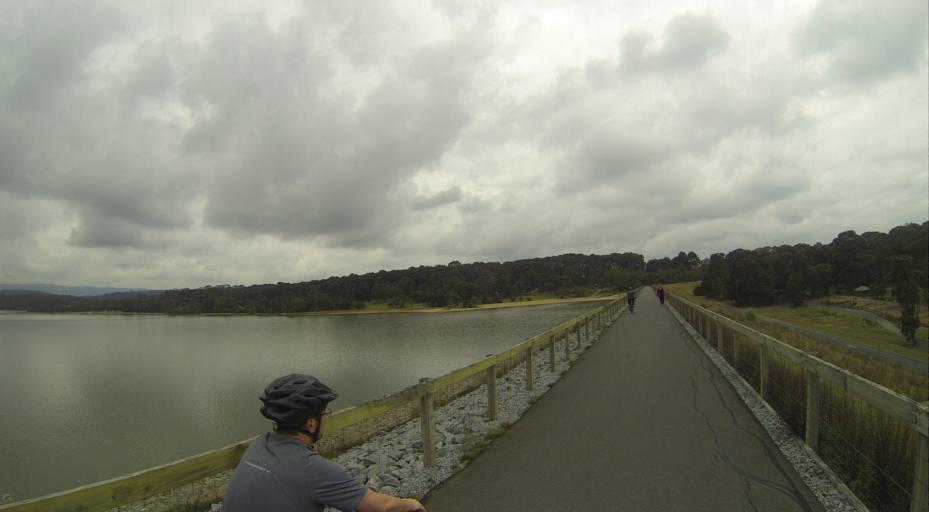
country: AU
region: Victoria
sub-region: Casey
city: Narre Warren North
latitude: -37.9706
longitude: 145.2972
